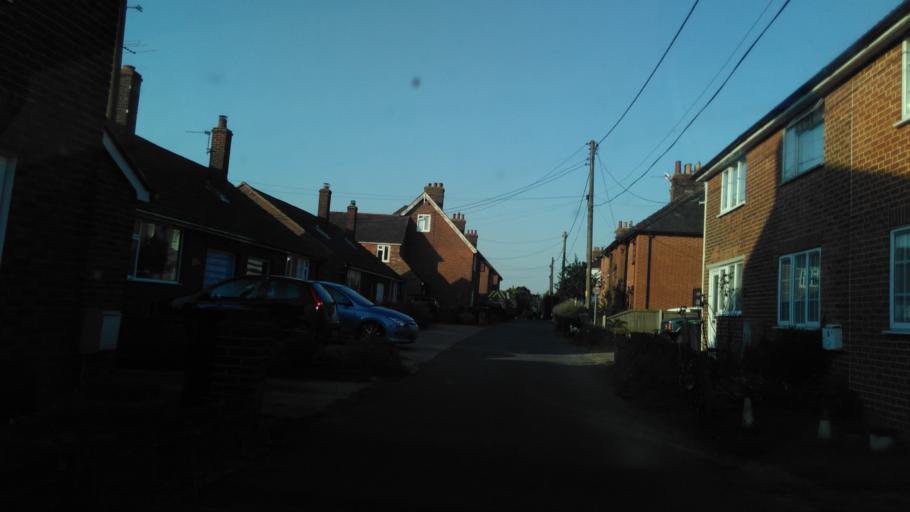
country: GB
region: England
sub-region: Kent
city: Chartham
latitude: 51.2702
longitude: 1.0152
